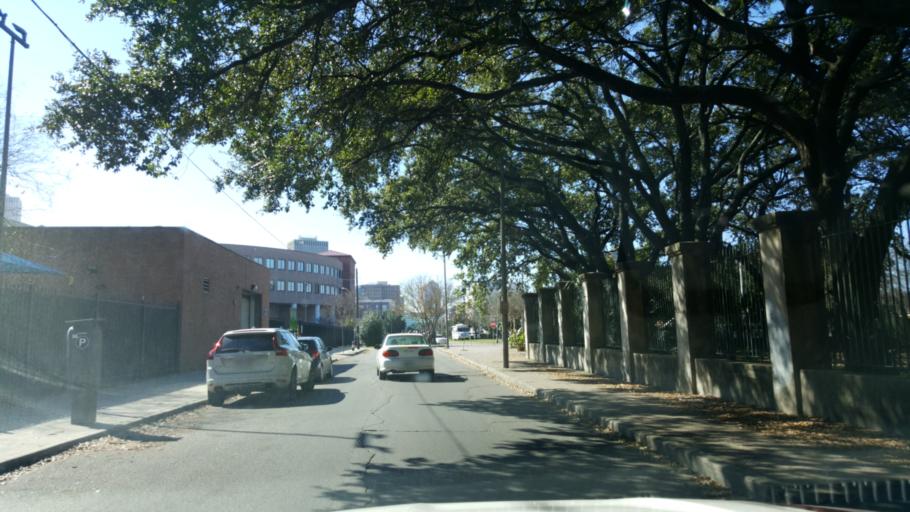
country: US
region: Louisiana
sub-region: Orleans Parish
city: New Orleans
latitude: 29.9608
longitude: -90.0691
